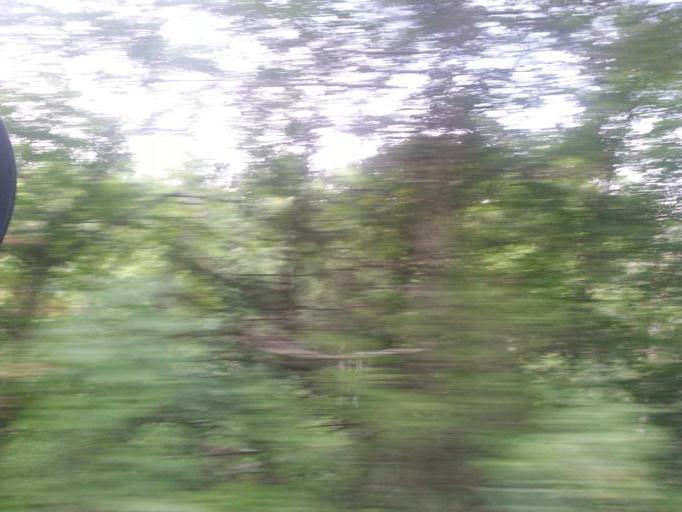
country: US
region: Tennessee
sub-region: Roane County
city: Oliver Springs
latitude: 36.1924
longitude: -84.3353
